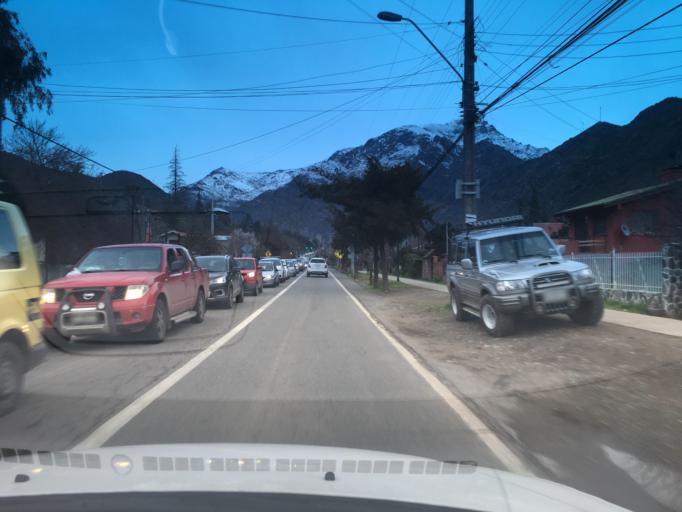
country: CL
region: Santiago Metropolitan
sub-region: Provincia de Cordillera
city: Puente Alto
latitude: -33.6977
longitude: -70.3346
